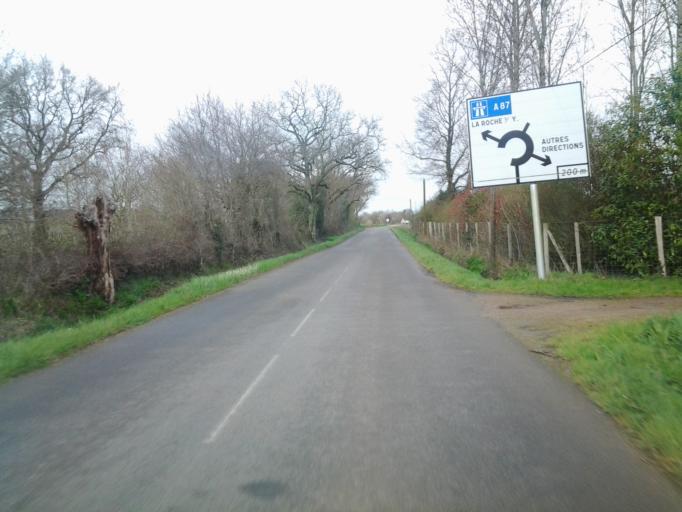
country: FR
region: Pays de la Loire
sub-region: Departement de la Vendee
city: Moutiers-les-Mauxfaits
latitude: 46.5017
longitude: -1.4445
